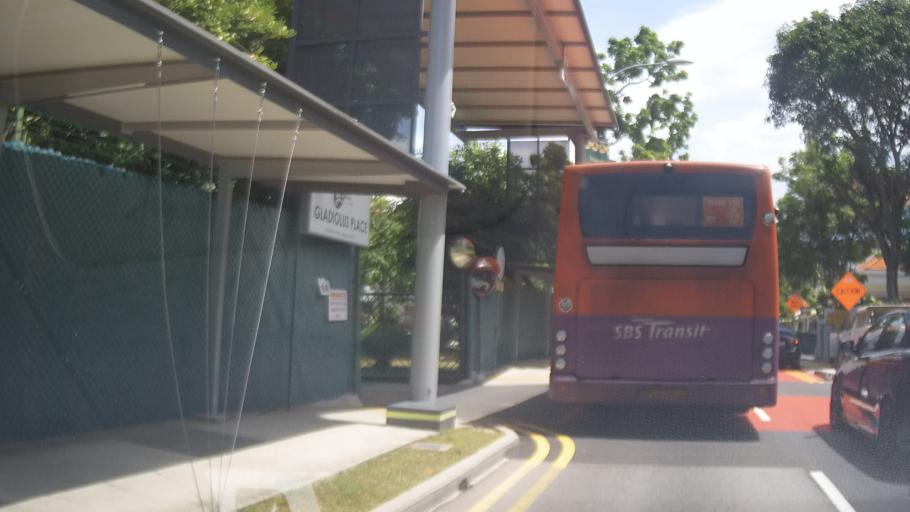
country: SG
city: Singapore
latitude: 1.3252
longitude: 103.8823
